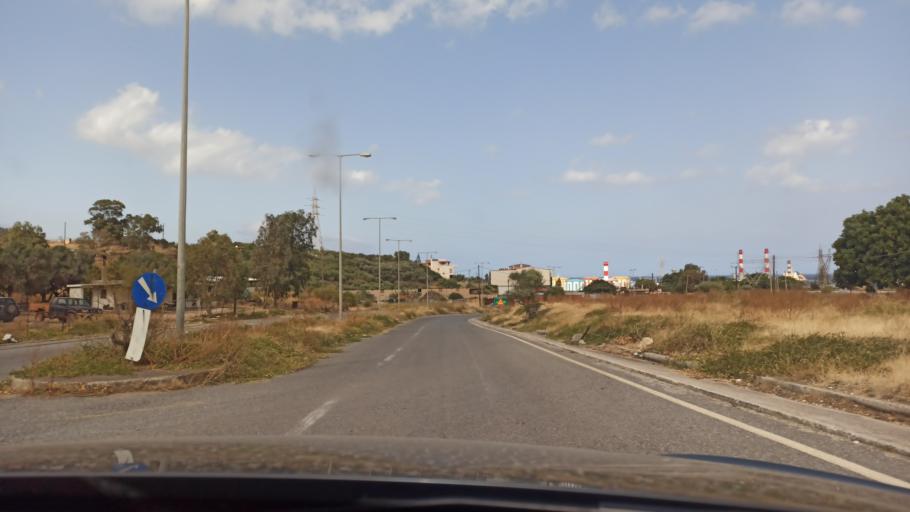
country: GR
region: Crete
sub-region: Nomos Irakleiou
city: Gazi
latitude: 35.3368
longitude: 25.0477
